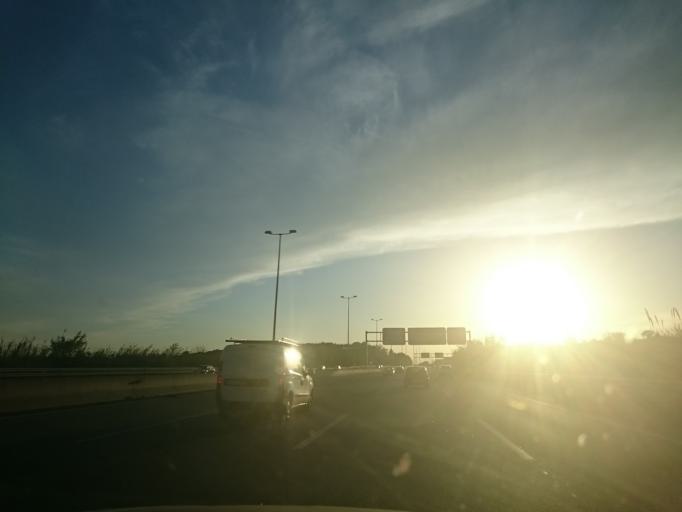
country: ES
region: Catalonia
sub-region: Provincia de Barcelona
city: Montmelo
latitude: 41.5590
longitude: 2.2577
